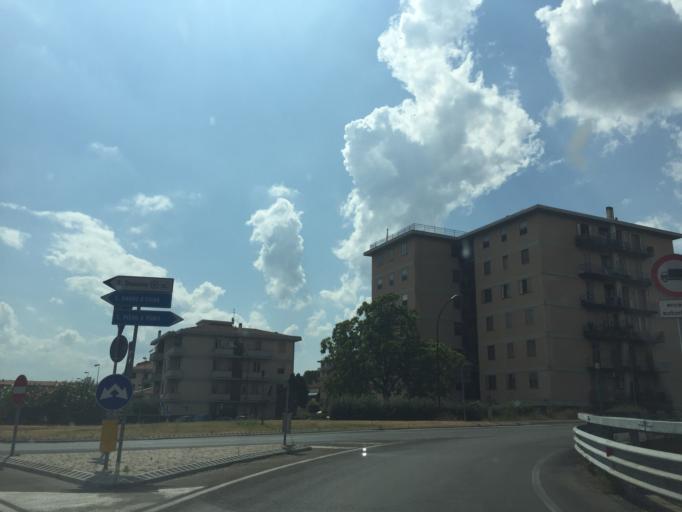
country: IT
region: Tuscany
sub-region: Province of Florence
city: San Donnino
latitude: 43.7997
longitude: 11.1417
